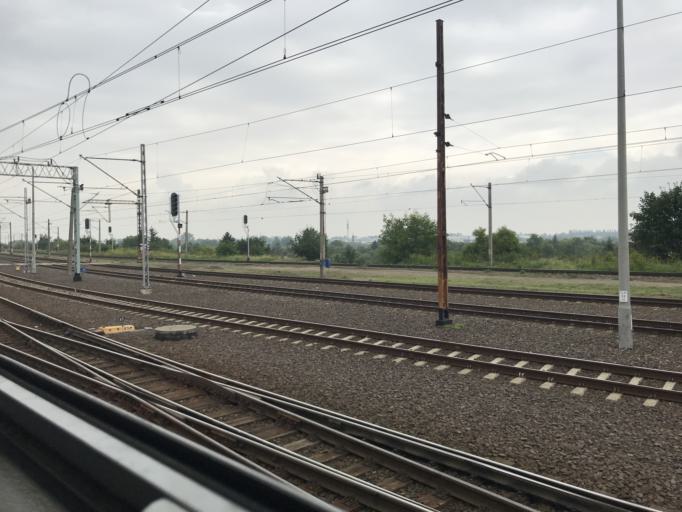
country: PL
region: Pomeranian Voivodeship
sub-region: Powiat tczewski
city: Tczew
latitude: 54.1005
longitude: 18.7866
